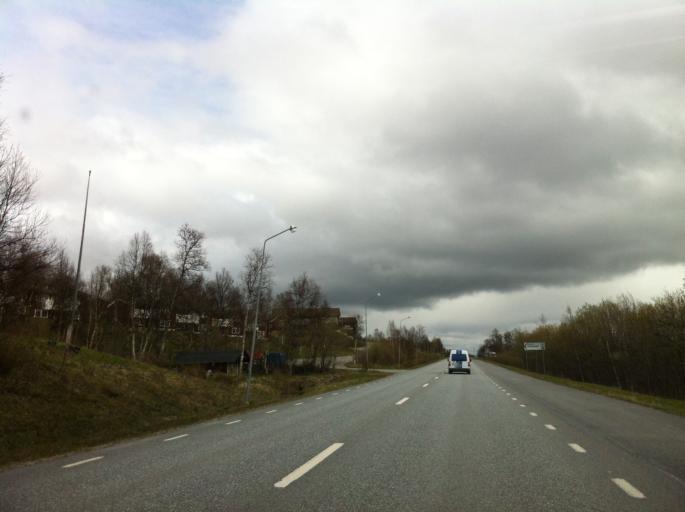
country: NO
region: Sor-Trondelag
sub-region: Tydal
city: Aas
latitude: 62.5487
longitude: 12.3128
